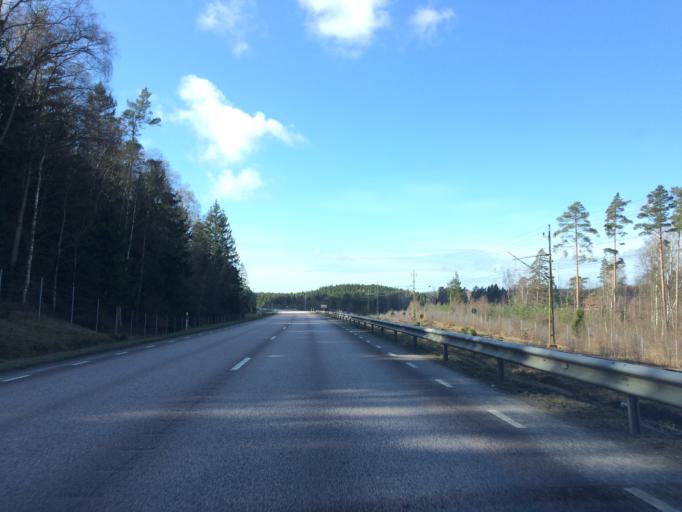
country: SE
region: Halland
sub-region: Laholms Kommun
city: Knared
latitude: 56.5206
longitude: 13.2742
